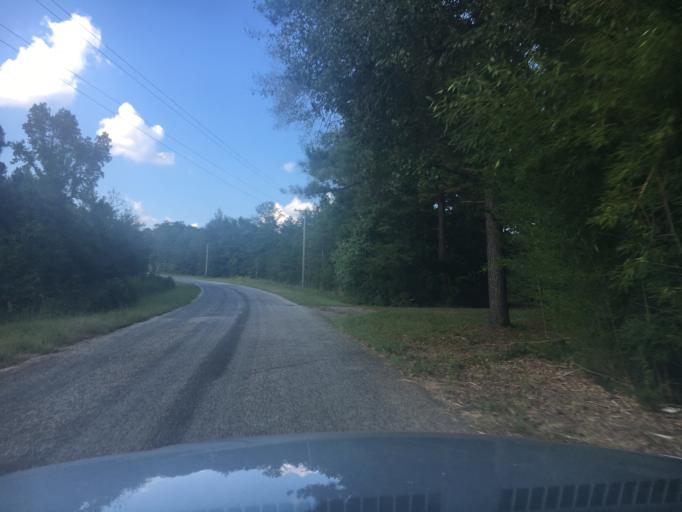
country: US
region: South Carolina
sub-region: Greenwood County
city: Ware Shoals
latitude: 34.5000
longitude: -82.2322
